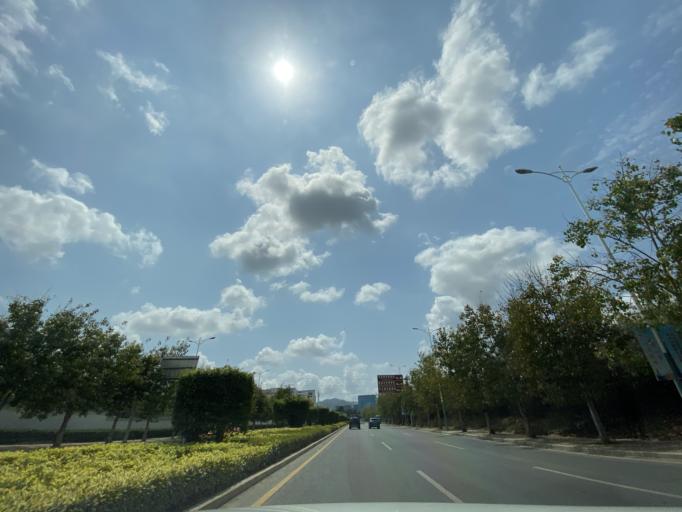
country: CN
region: Hainan
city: Tiandu
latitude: 18.3212
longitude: 109.5253
